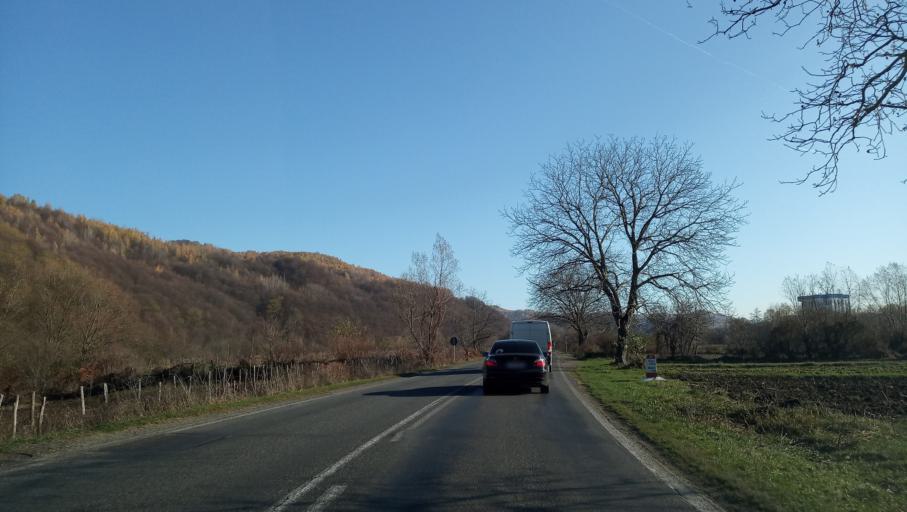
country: RO
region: Caras-Severin
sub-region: Comuna Zavoi
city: Zavoi
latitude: 45.5291
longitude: 22.4355
